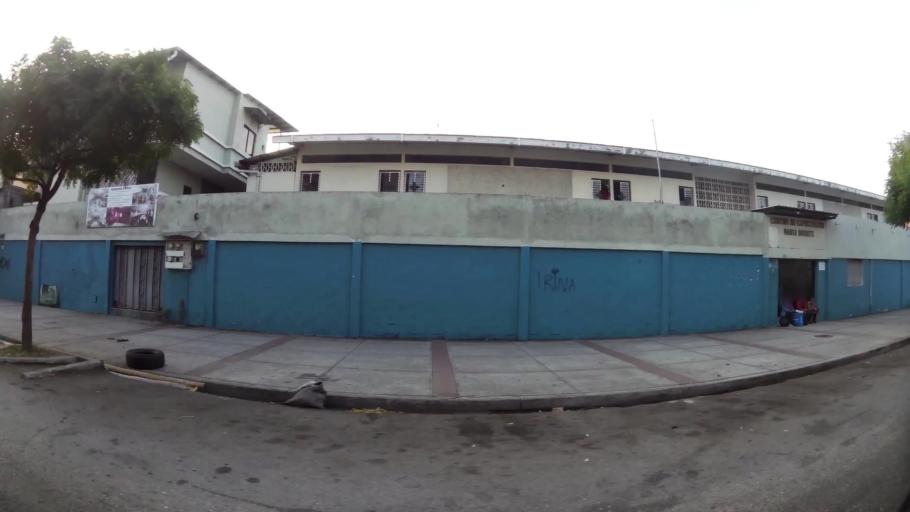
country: EC
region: Guayas
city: Guayaquil
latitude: -2.1982
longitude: -79.8972
